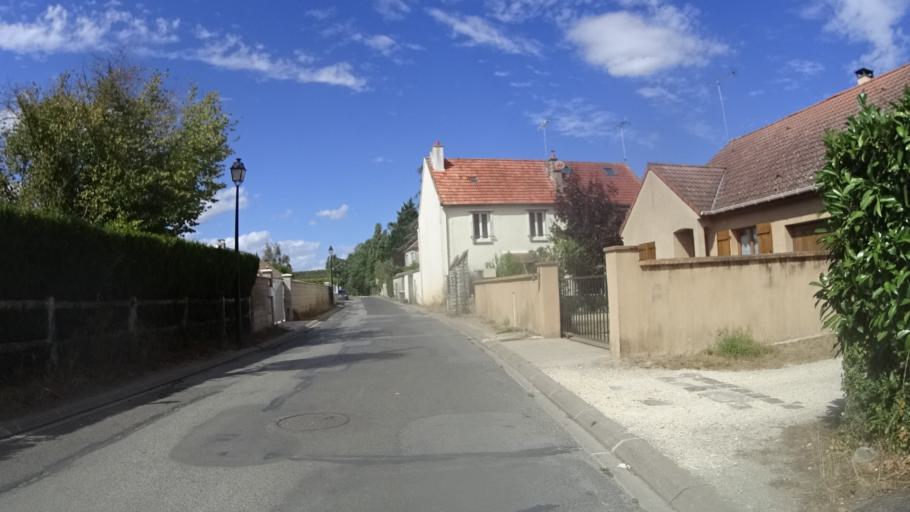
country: FR
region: Ile-de-France
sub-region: Departement de l'Essonne
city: Boutigny-sur-Essonne
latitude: 48.4196
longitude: 2.3906
